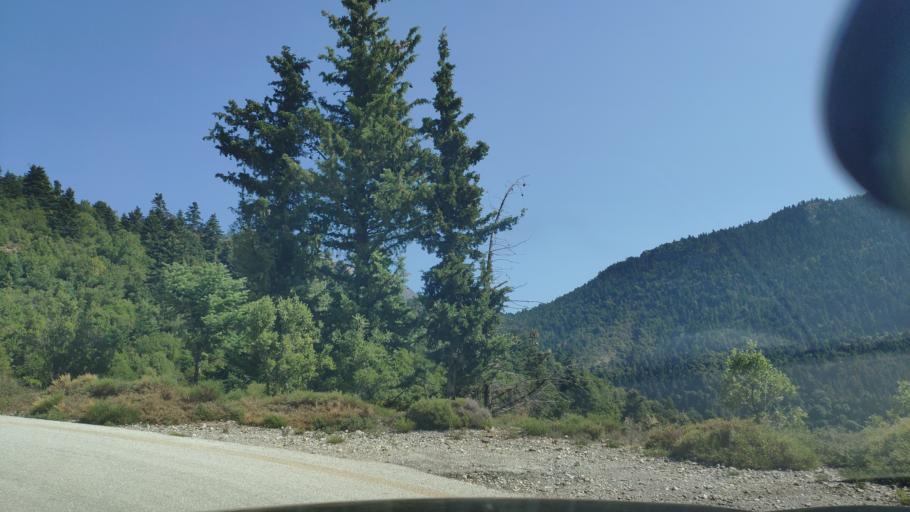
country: GR
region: Peloponnese
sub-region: Nomos Korinthias
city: Nemea
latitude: 37.8614
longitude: 22.3825
